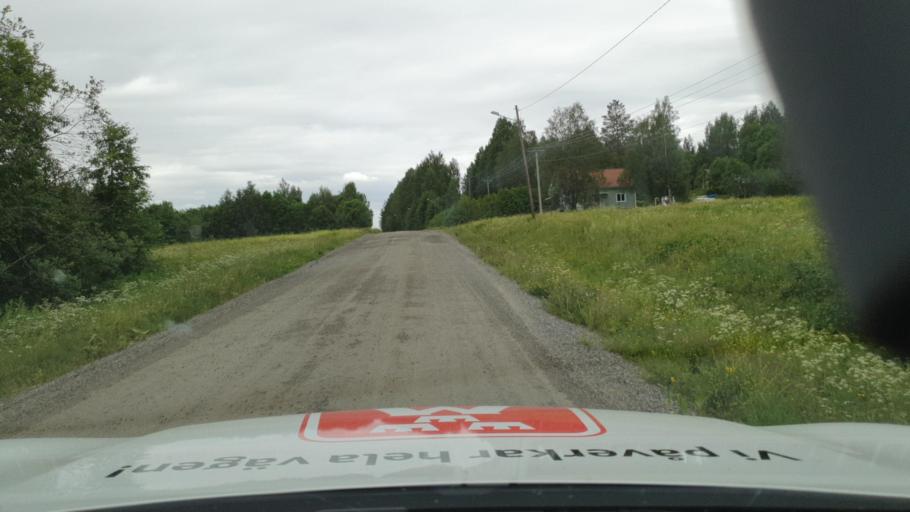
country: SE
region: Vaesterbotten
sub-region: Bjurholms Kommun
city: Bjurholm
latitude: 63.7786
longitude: 19.3932
